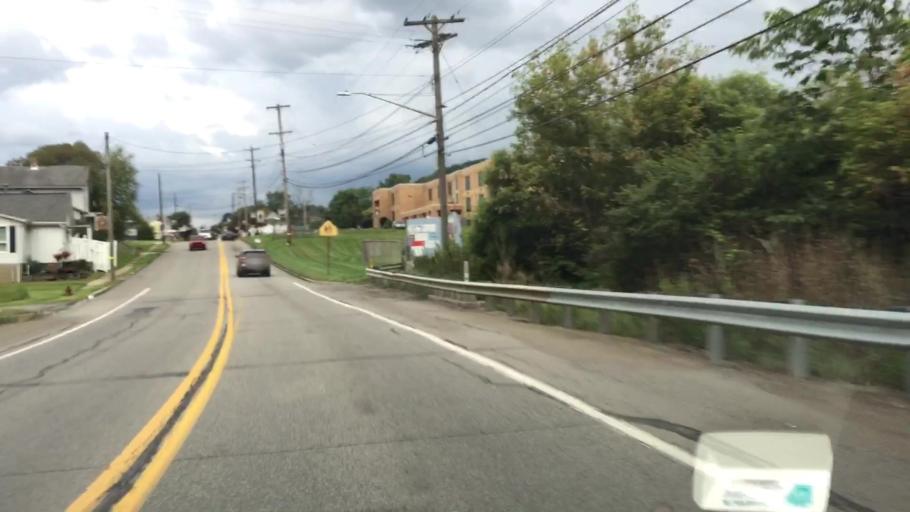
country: US
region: Pennsylvania
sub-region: Butler County
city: Evans City
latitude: 40.7705
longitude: -80.0713
